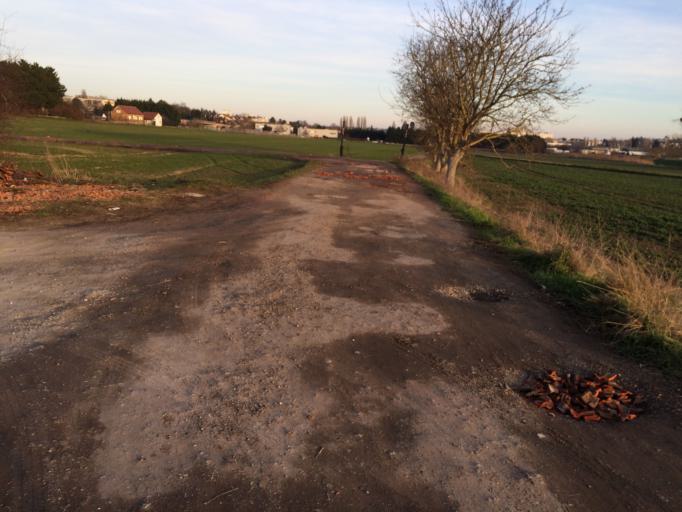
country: FR
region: Ile-de-France
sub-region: Departement de l'Essonne
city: Champlan
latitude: 48.7018
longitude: 2.2793
